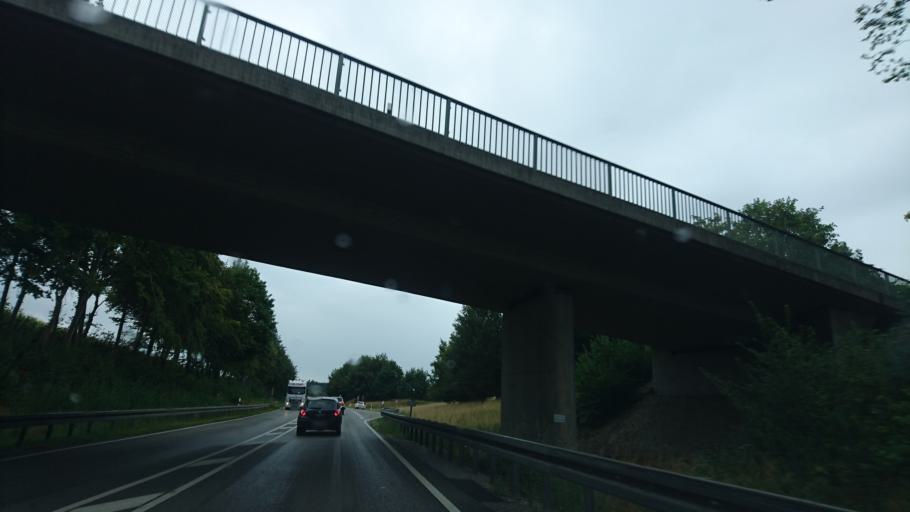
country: DE
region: Bavaria
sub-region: Swabia
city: Kuhbach
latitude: 48.4939
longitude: 11.2046
